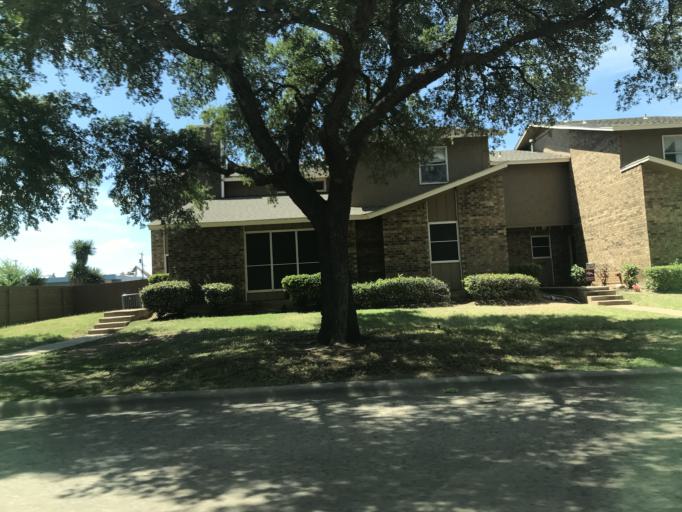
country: US
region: Texas
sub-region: Taylor County
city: Abilene
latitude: 32.4210
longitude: -99.7620
